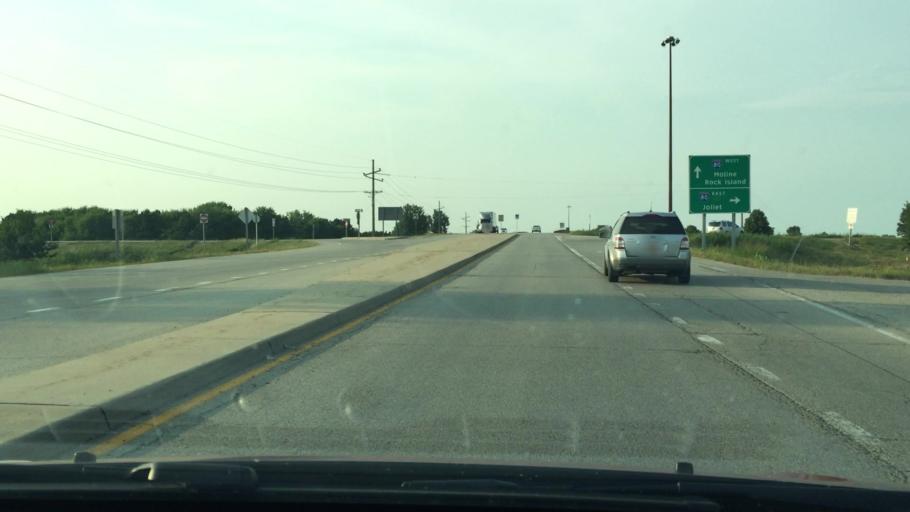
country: US
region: Illinois
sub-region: Bureau County
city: Ladd
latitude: 41.3649
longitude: -89.2186
